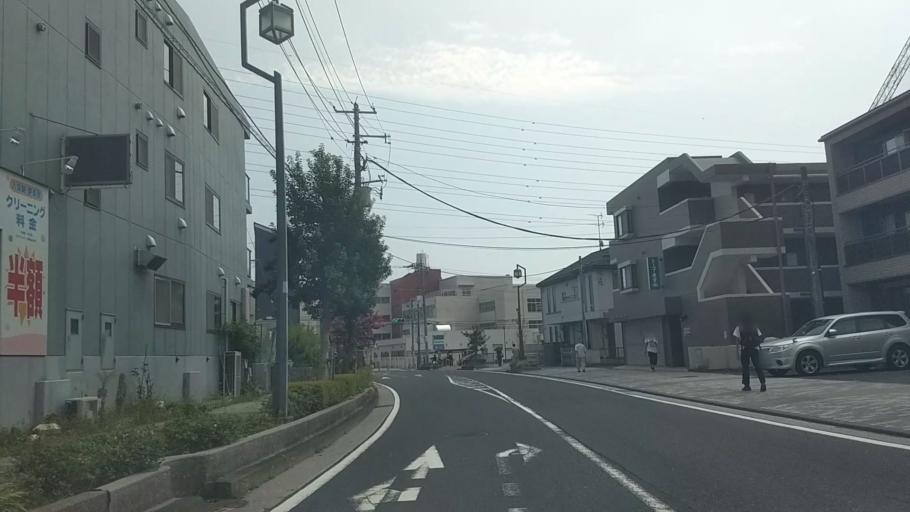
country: JP
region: Kanagawa
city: Yokohama
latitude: 35.4891
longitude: 139.6082
